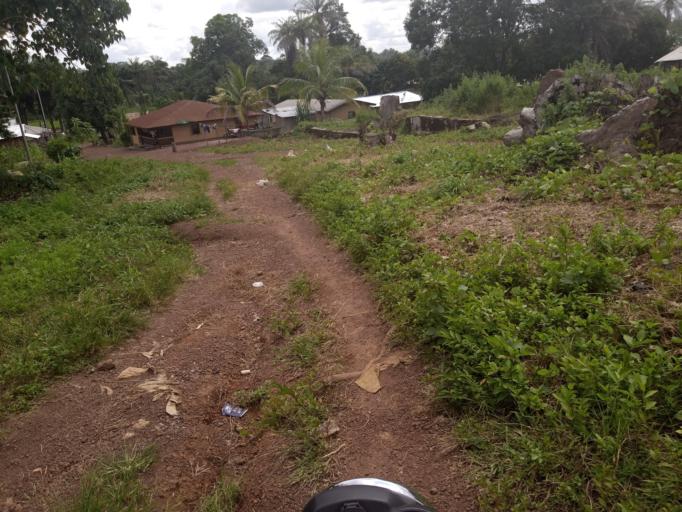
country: SL
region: Northern Province
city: Kamakwie
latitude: 9.4923
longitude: -12.2443
